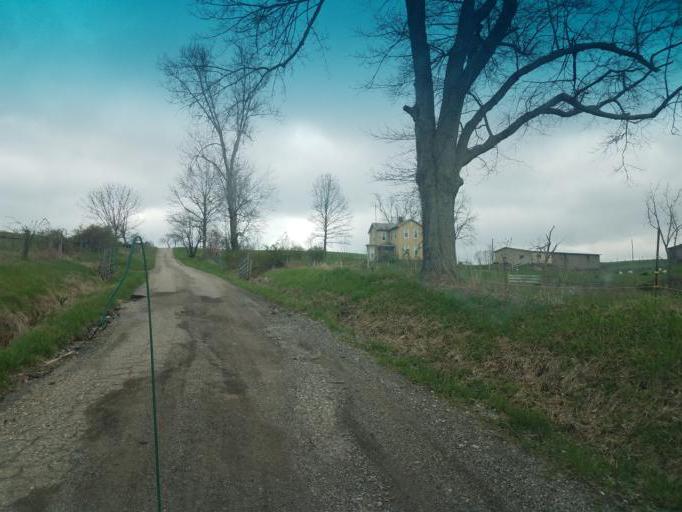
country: US
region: Ohio
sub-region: Stark County
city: Beach City
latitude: 40.6135
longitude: -81.6021
